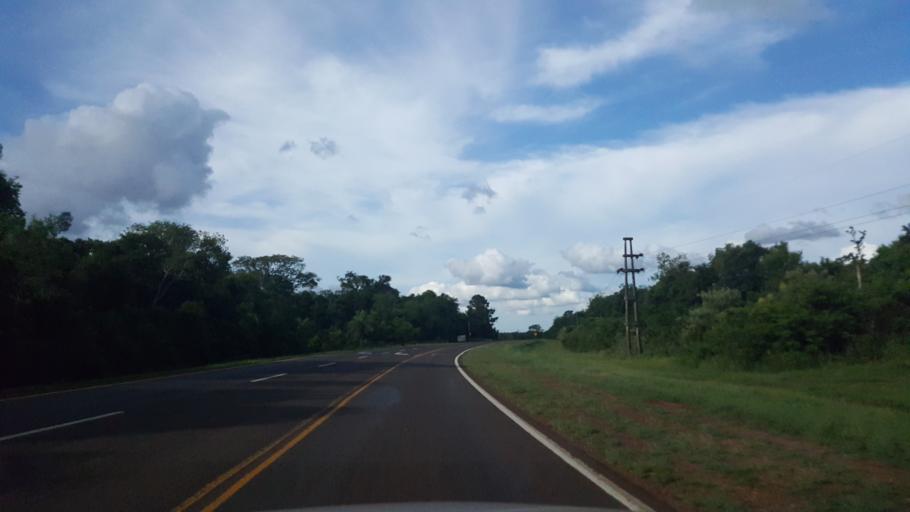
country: AR
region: Misiones
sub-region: Departamento de Candelaria
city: Loreto
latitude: -27.3332
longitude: -55.5435
